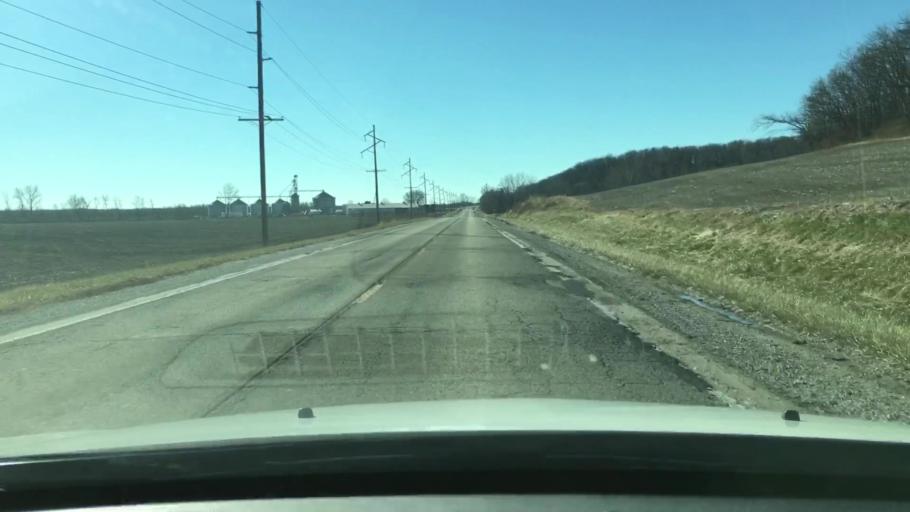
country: US
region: Illinois
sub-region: Fulton County
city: Astoria
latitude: 40.1717
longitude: -90.2892
